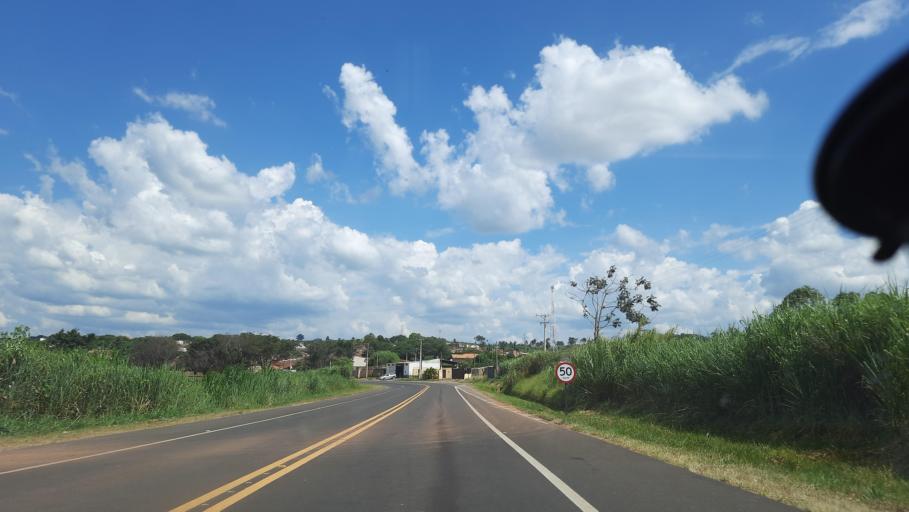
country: BR
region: Sao Paulo
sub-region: Sao Jose Do Rio Pardo
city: Sao Jose do Rio Pardo
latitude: -21.6056
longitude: -46.9372
